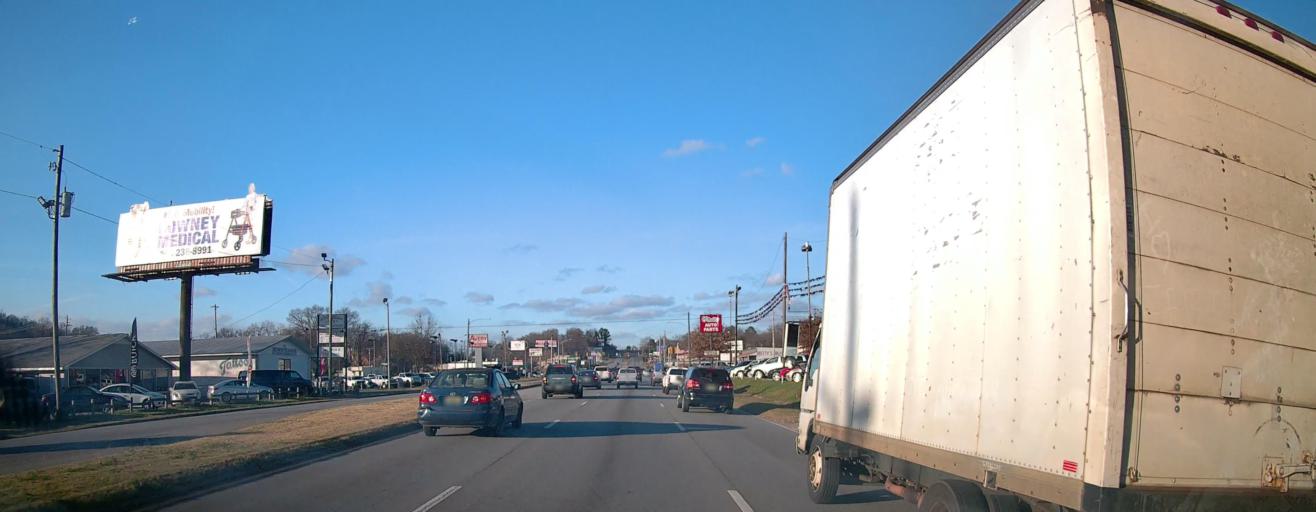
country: US
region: Alabama
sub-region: Calhoun County
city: Anniston
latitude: 33.6401
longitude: -85.8256
